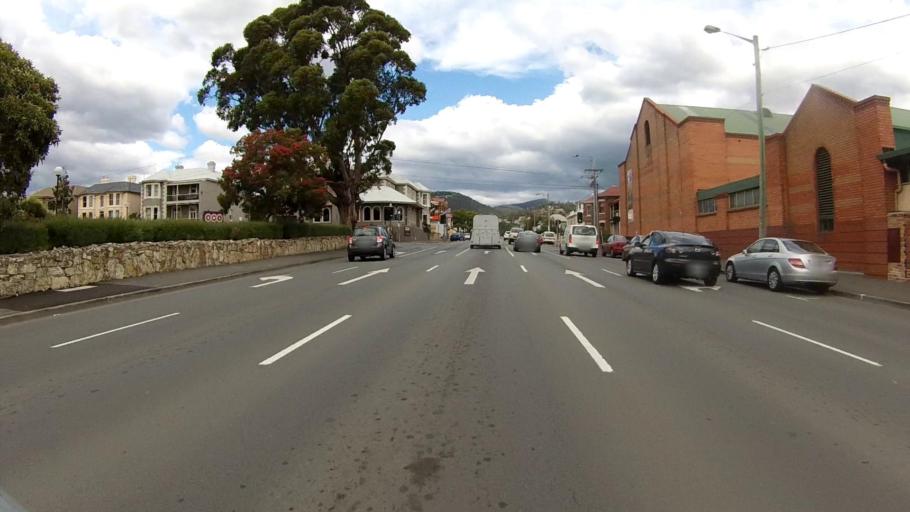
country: AU
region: Tasmania
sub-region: Hobart
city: Sandy Bay
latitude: -42.8888
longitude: 147.3241
